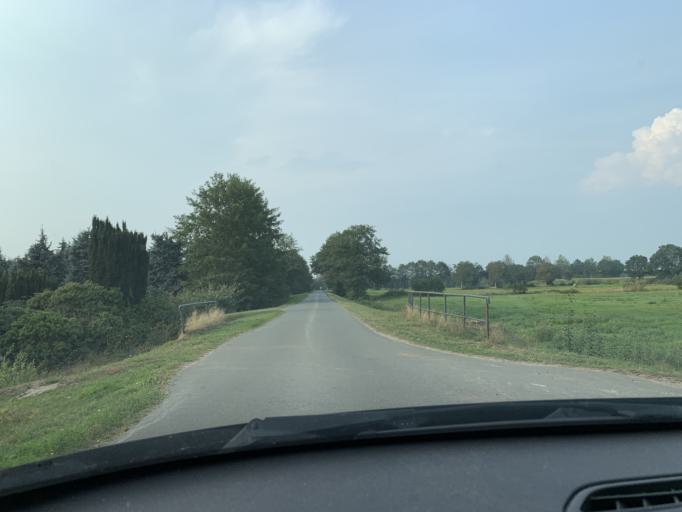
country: DE
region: Lower Saxony
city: Apen
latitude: 53.2336
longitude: 7.8180
